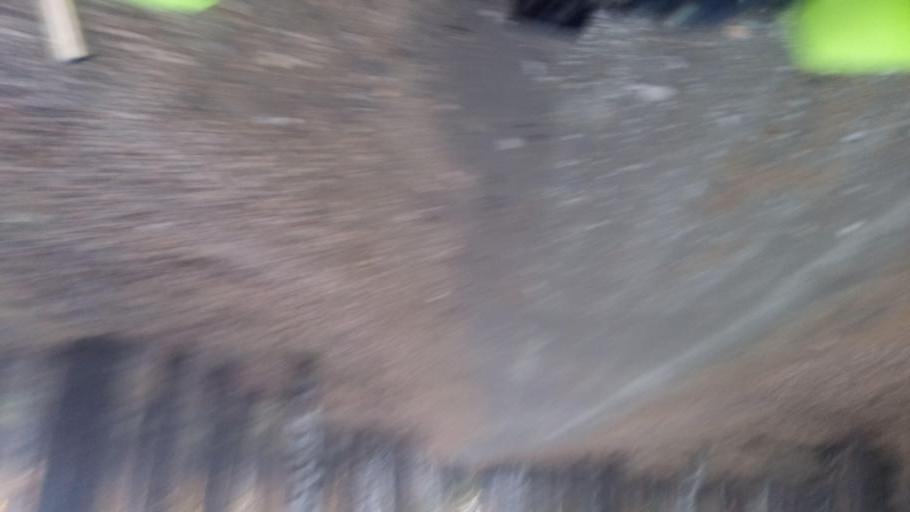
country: RU
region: Chelyabinsk
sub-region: Gorod Chelyabinsk
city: Chelyabinsk
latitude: 55.1244
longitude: 61.3458
